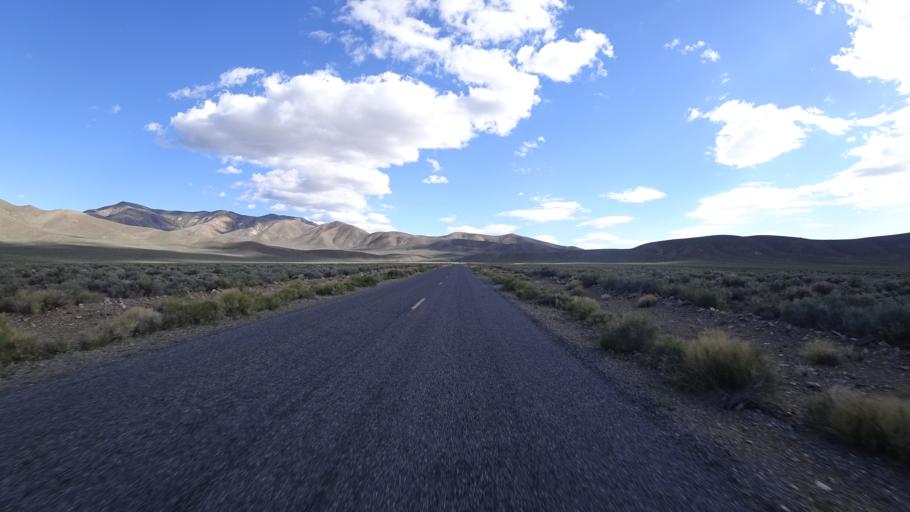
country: US
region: California
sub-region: San Bernardino County
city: Searles Valley
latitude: 36.3472
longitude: -117.1350
